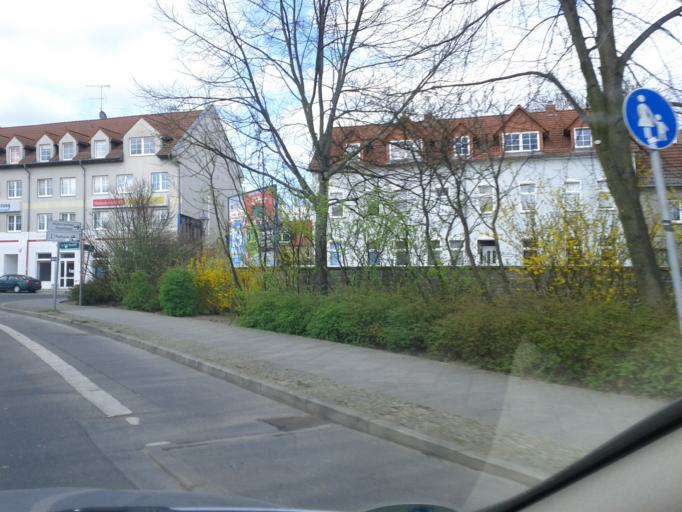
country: DE
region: Brandenburg
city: Furstenwalde
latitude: 52.3566
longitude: 14.0625
